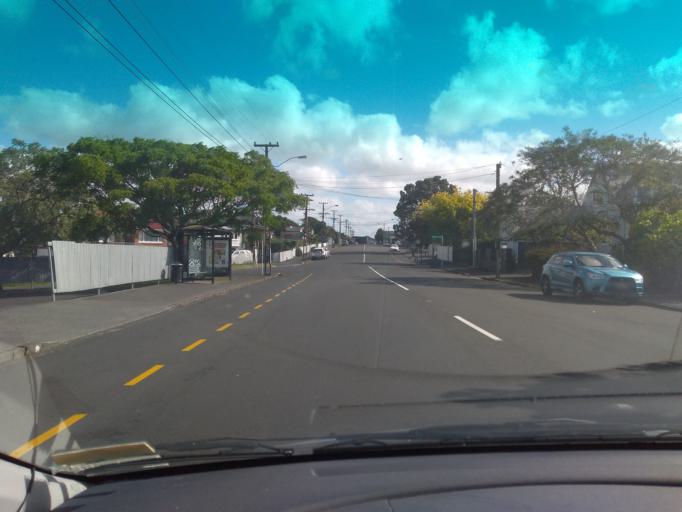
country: NZ
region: Auckland
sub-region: Auckland
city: Rosebank
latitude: -36.8566
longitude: 174.7035
